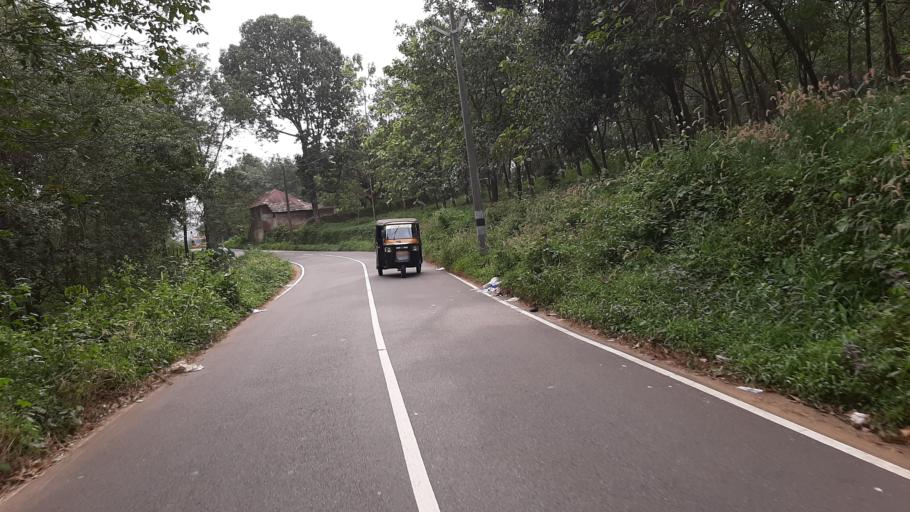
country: IN
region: Kerala
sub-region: Pattanamtitta
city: Pathanamthitta
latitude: 9.4594
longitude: 76.8693
